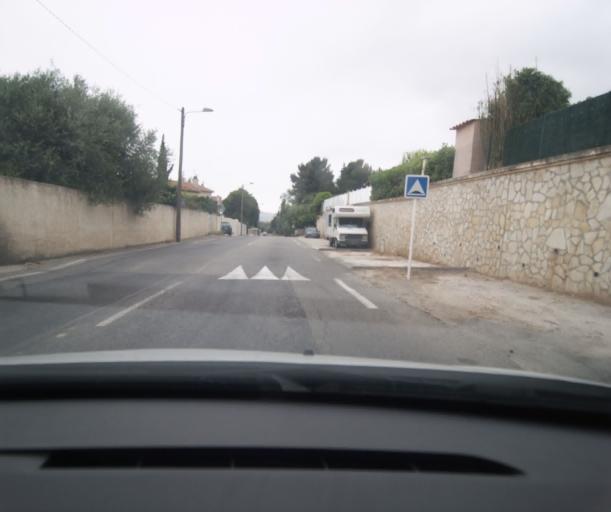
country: FR
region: Provence-Alpes-Cote d'Azur
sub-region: Departement du Var
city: La Valette-du-Var
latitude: 43.1443
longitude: 5.9801
